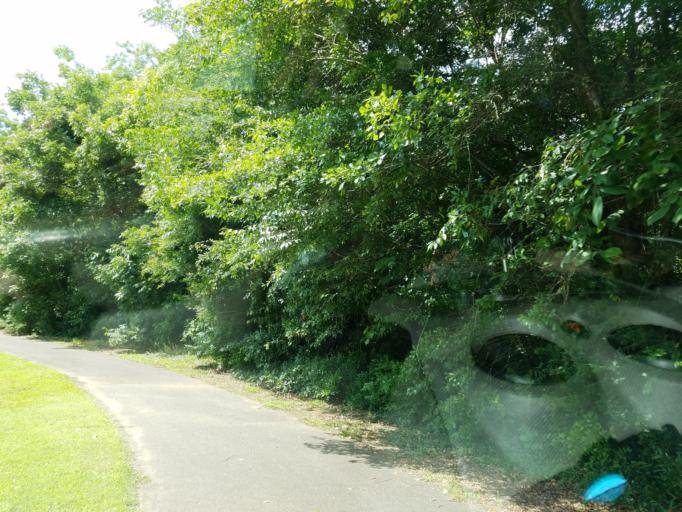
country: US
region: Georgia
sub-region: Cherokee County
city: Ball Ground
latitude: 34.3361
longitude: -84.3764
